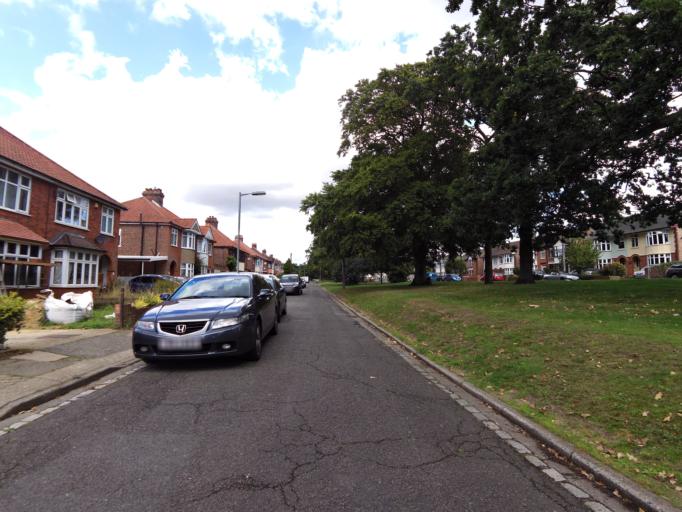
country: GB
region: England
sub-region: Suffolk
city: Ipswich
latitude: 52.0407
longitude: 1.1800
